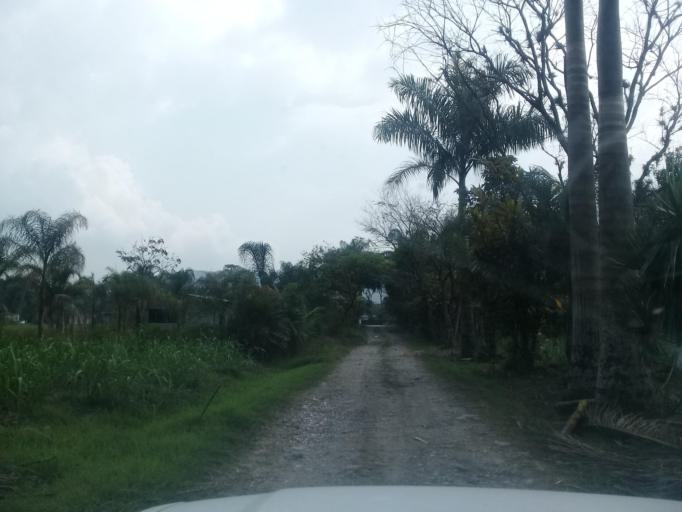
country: MX
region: Veracruz
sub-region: Ixtaczoquitlan
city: Capoluca
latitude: 18.8182
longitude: -96.9946
